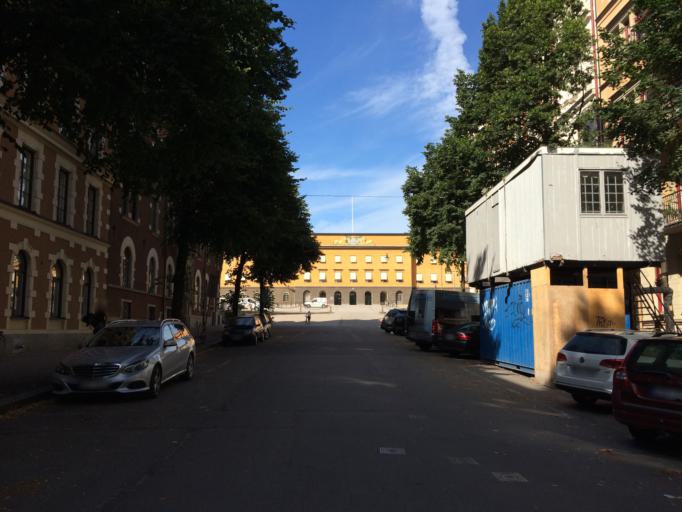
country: SE
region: Stockholm
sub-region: Stockholms Kommun
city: OEstermalm
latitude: 59.3332
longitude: 18.0894
